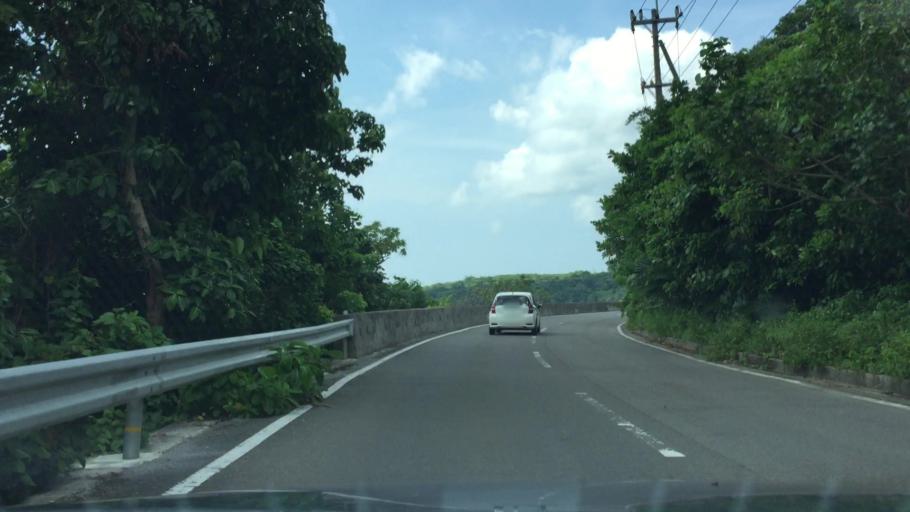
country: JP
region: Okinawa
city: Ishigaki
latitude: 24.4613
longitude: 124.2262
